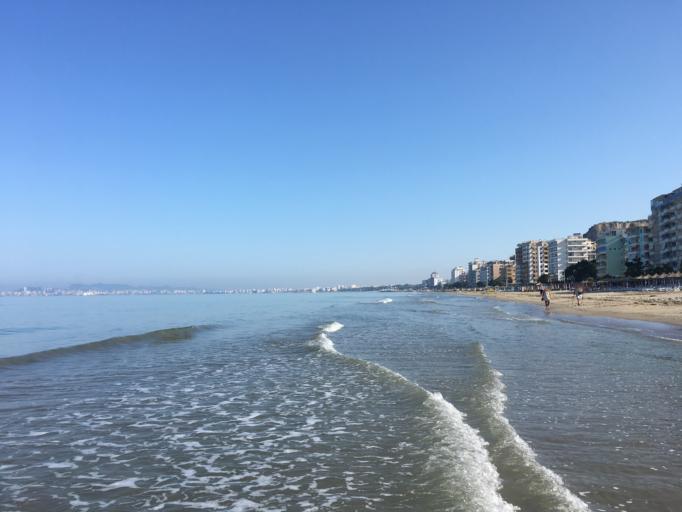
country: AL
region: Tirane
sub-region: Rrethi i Kavajes
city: Golem
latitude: 41.2718
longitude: 19.5163
